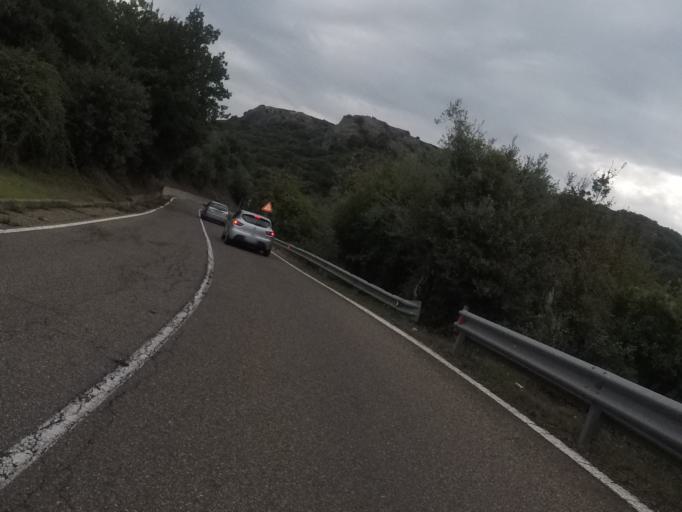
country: IT
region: Sardinia
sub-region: Provincia di Oristano
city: Sennariolo
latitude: 40.2127
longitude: 8.5600
